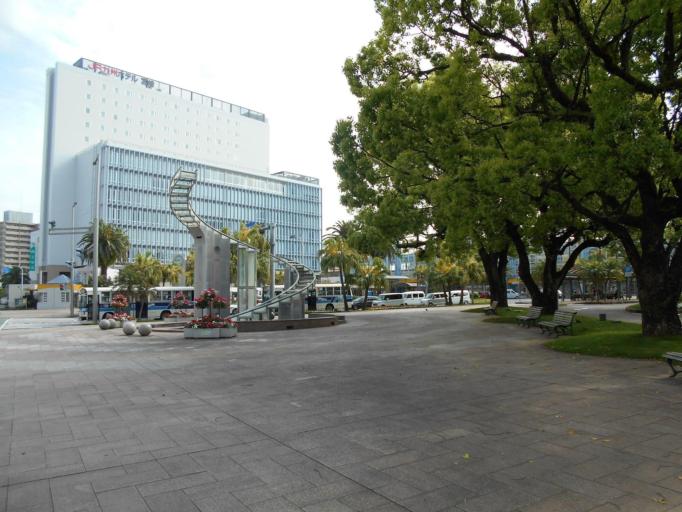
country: JP
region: Miyazaki
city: Miyazaki-shi
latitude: 31.9155
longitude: 131.4307
